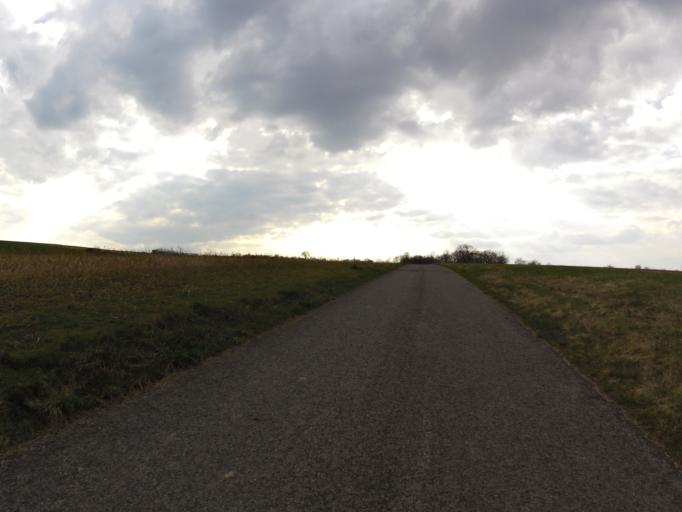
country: DE
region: Bavaria
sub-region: Regierungsbezirk Unterfranken
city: Buchbrunn
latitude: 49.7457
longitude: 10.1276
